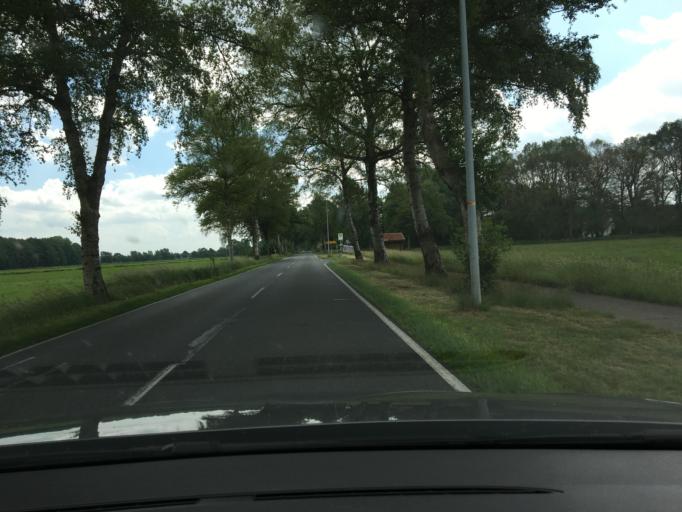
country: DE
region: Lower Saxony
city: Tarmstedt
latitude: 53.2468
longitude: 9.0182
